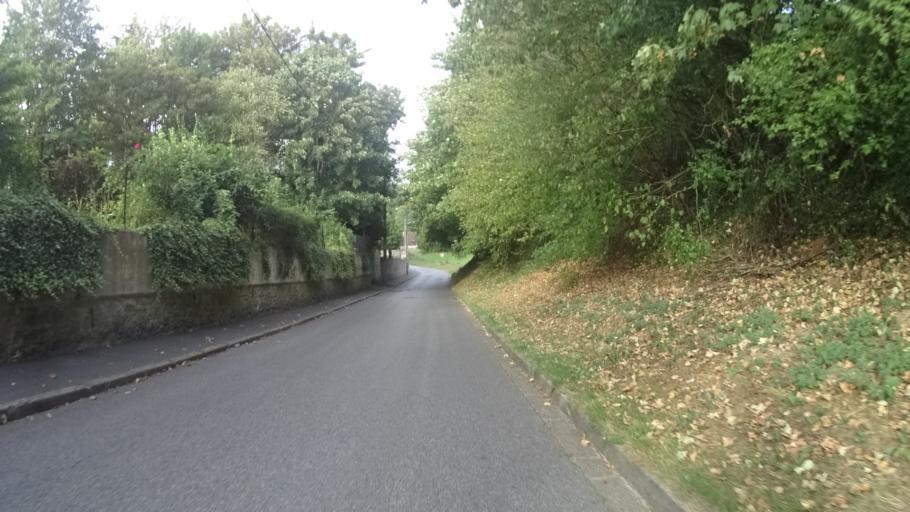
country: FR
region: Picardie
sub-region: Departement de l'Oise
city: Ver-sur-Launette
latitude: 49.1266
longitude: 2.6990
